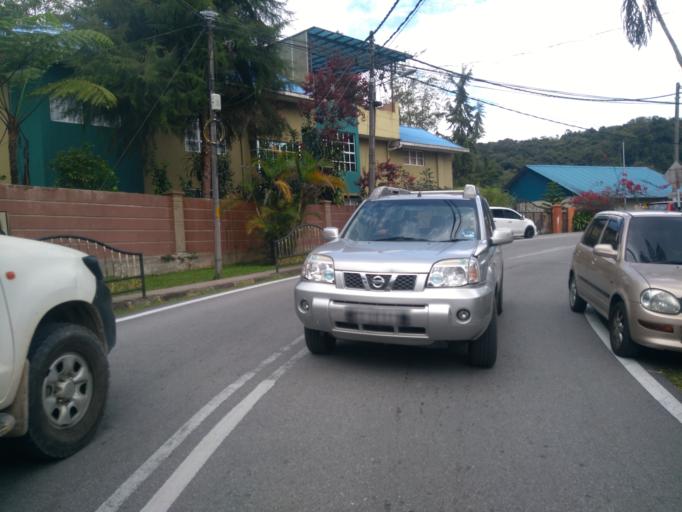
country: MY
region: Pahang
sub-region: Cameron Highlands
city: Tanah Rata
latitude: 4.4774
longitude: 101.3818
